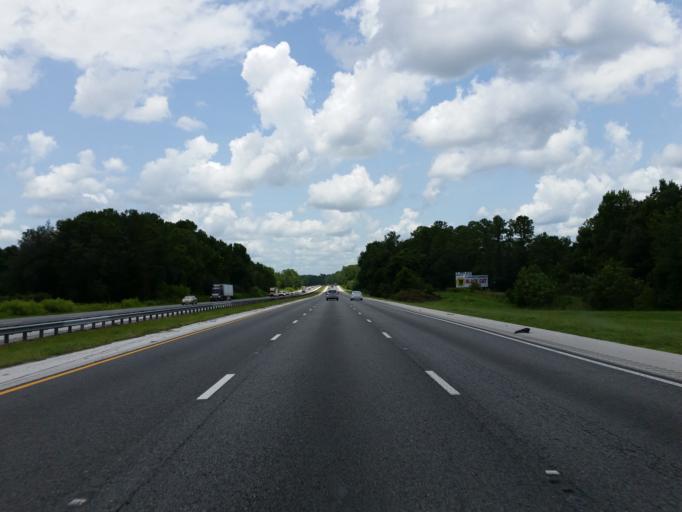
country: US
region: Florida
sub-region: Marion County
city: Citra
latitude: 29.4525
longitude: -82.2686
